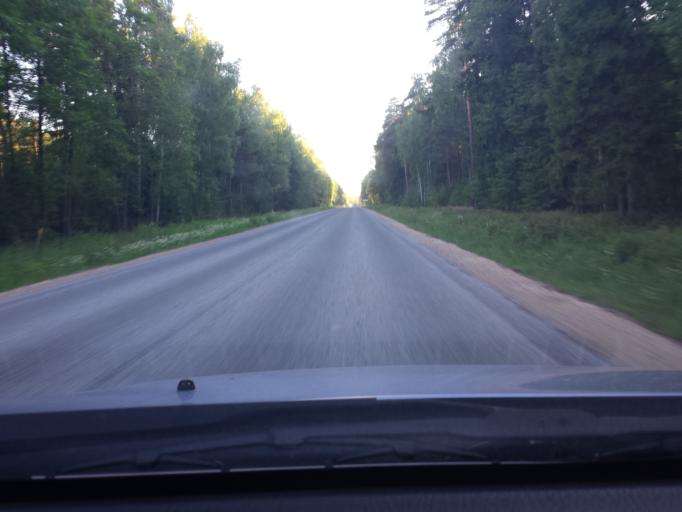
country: LV
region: Carnikava
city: Carnikava
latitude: 57.1062
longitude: 24.2176
